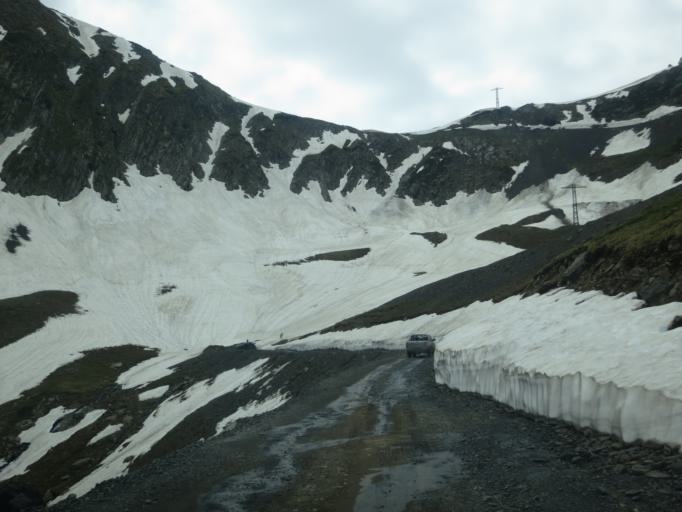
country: GE
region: Kakheti
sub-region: Telavi
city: Telavi
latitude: 42.2838
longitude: 45.5089
